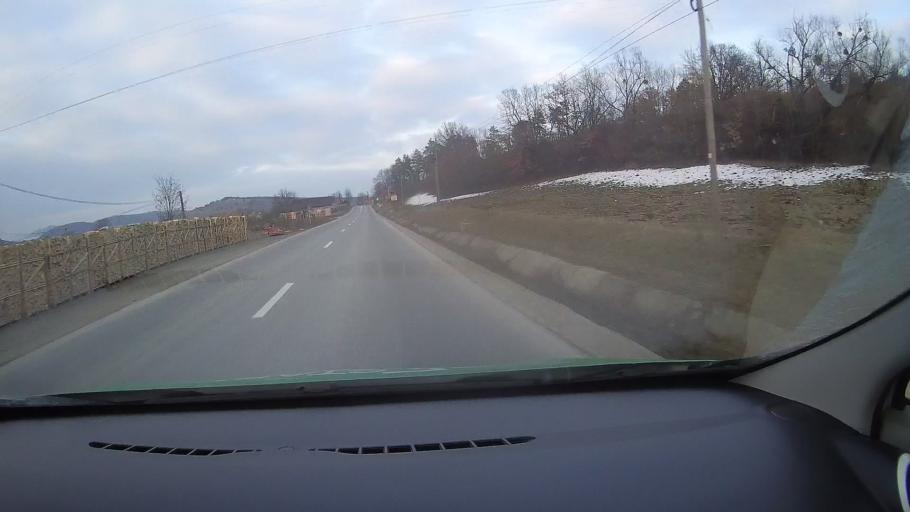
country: RO
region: Harghita
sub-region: Comuna Simonesti
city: Simonesti
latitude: 46.3512
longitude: 25.1300
